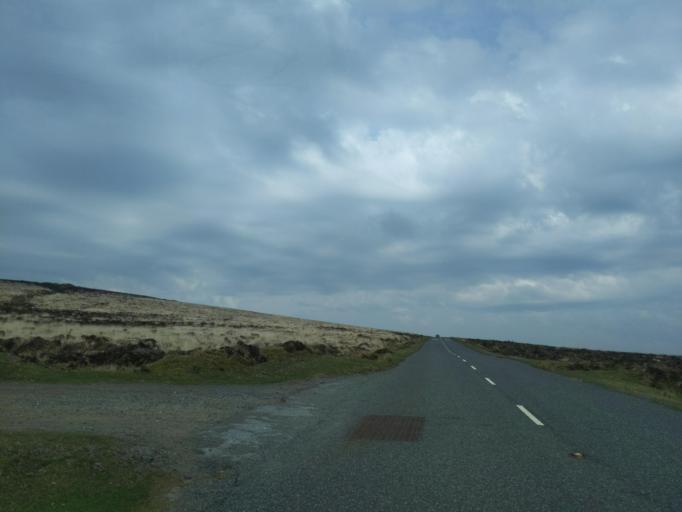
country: GB
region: England
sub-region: Devon
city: Ashburton
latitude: 50.6096
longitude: -3.8834
